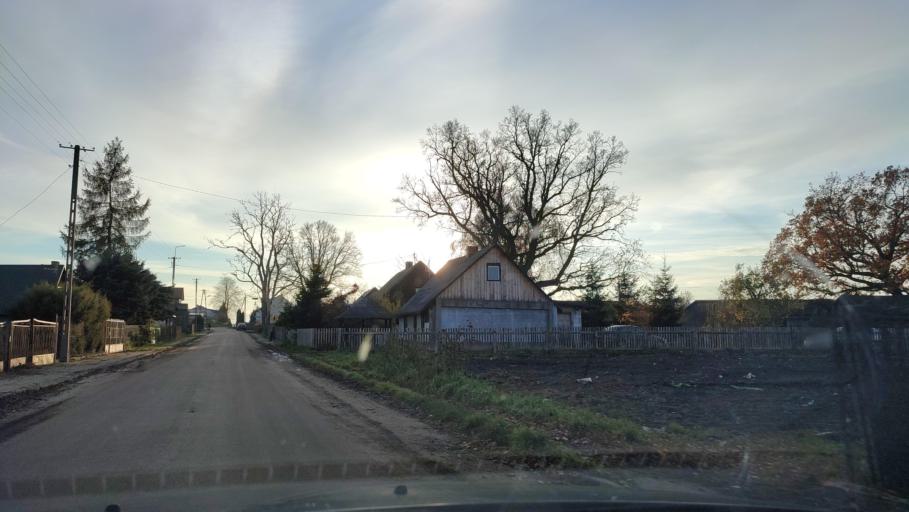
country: PL
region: Masovian Voivodeship
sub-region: Powiat mlawski
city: Dzierzgowo
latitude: 53.2801
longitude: 20.6475
